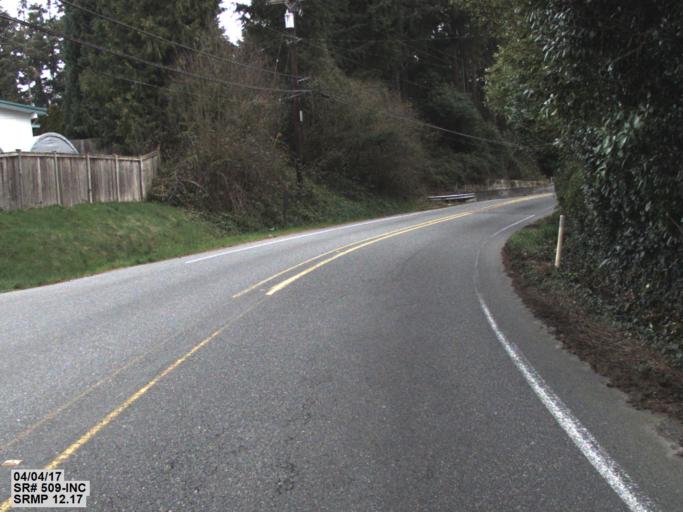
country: US
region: Washington
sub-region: King County
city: Federal Way
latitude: 47.3303
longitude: -122.3478
